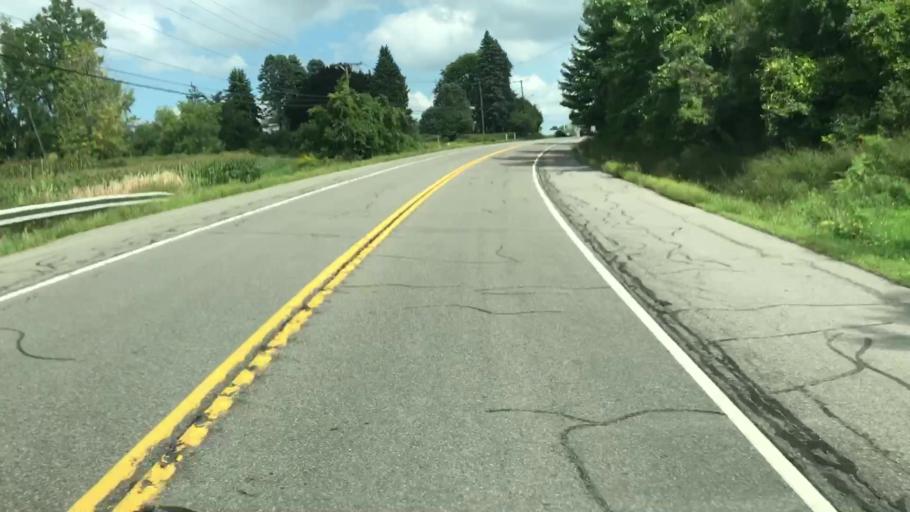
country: US
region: New York
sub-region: Onondaga County
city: Westvale
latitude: 42.9936
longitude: -76.2279
